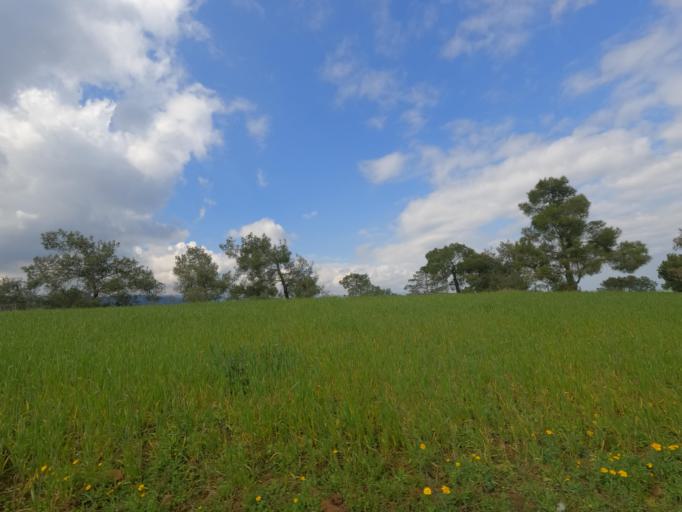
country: CY
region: Lefkosia
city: Astromeritis
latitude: 35.0764
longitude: 32.9615
